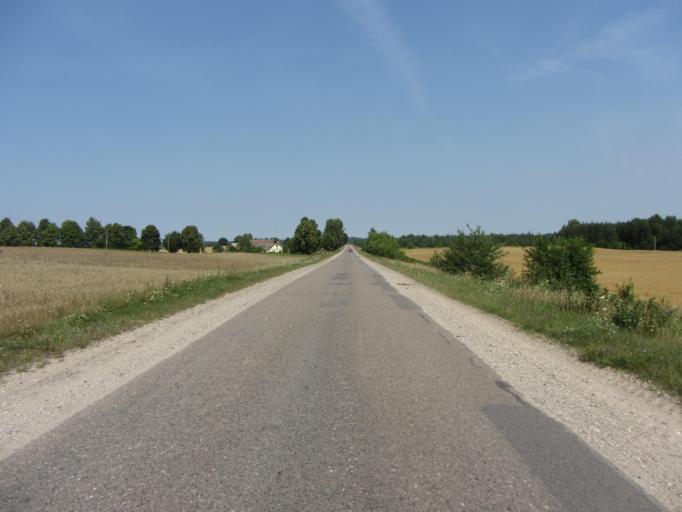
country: LT
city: Veisiejai
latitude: 54.0543
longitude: 23.6524
